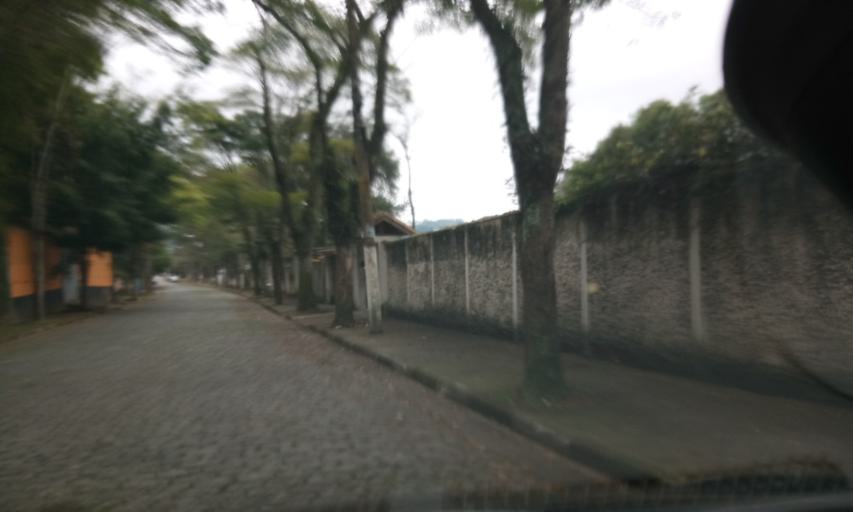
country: BR
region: Sao Paulo
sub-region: Sao Bernardo Do Campo
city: Sao Bernardo do Campo
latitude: -23.7809
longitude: -46.5339
